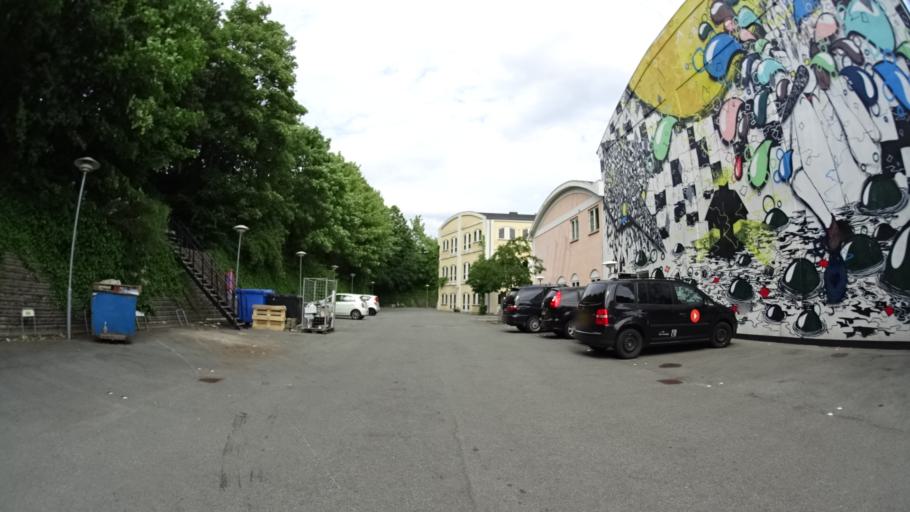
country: DK
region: Central Jutland
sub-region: Arhus Kommune
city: Arhus
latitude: 56.1540
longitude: 10.1757
